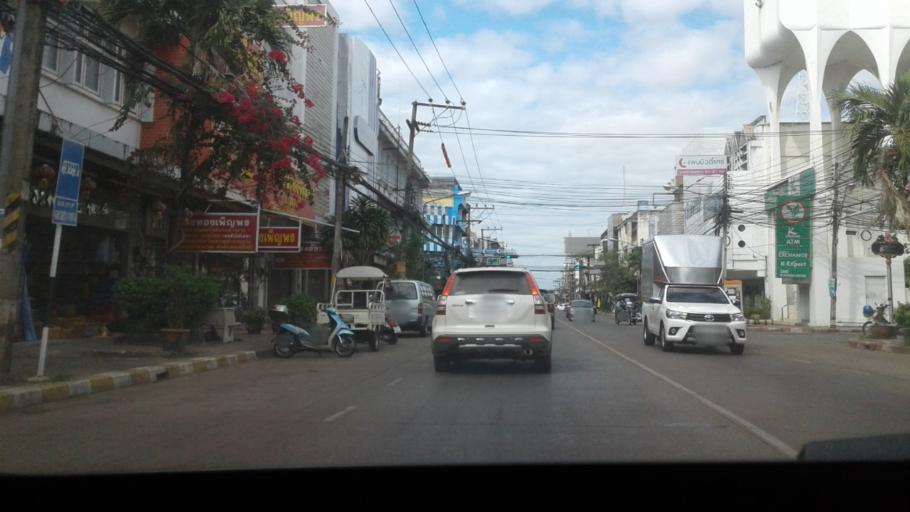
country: TH
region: Changwat Udon Thani
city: Udon Thani
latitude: 17.4070
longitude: 102.7889
